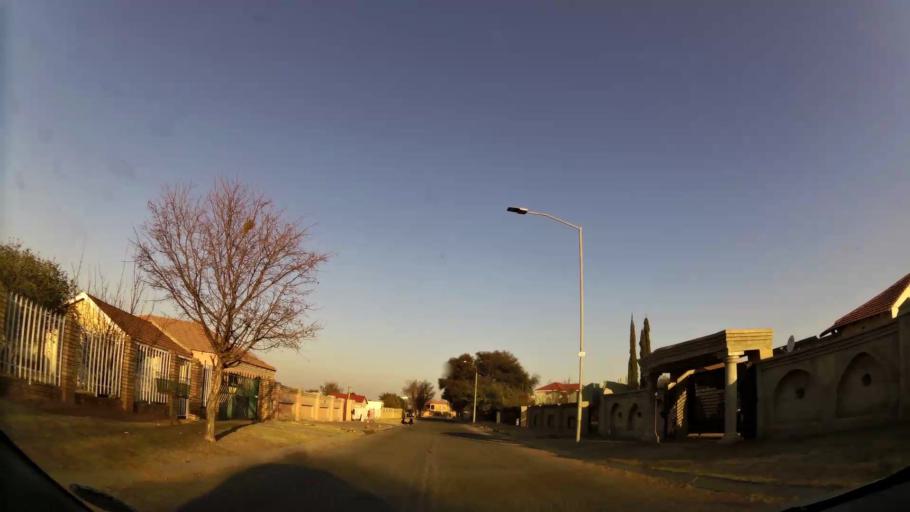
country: ZA
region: Gauteng
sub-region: West Rand District Municipality
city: Randfontein
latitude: -26.2041
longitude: 27.6579
